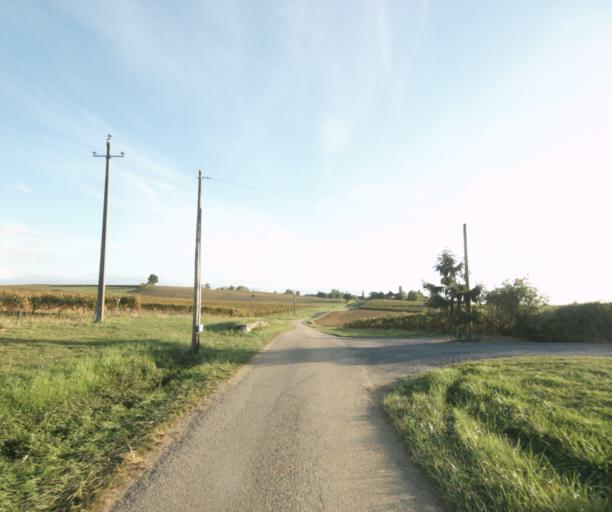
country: FR
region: Midi-Pyrenees
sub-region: Departement du Gers
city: Gondrin
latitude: 43.8565
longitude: 0.2993
